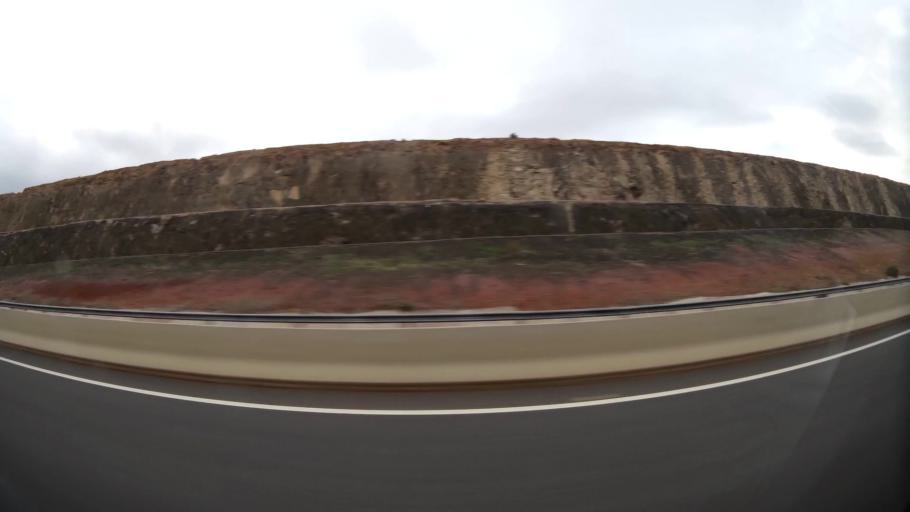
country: MA
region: Taza-Al Hoceima-Taounate
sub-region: Taza
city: Guercif
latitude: 34.3912
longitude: -3.2162
